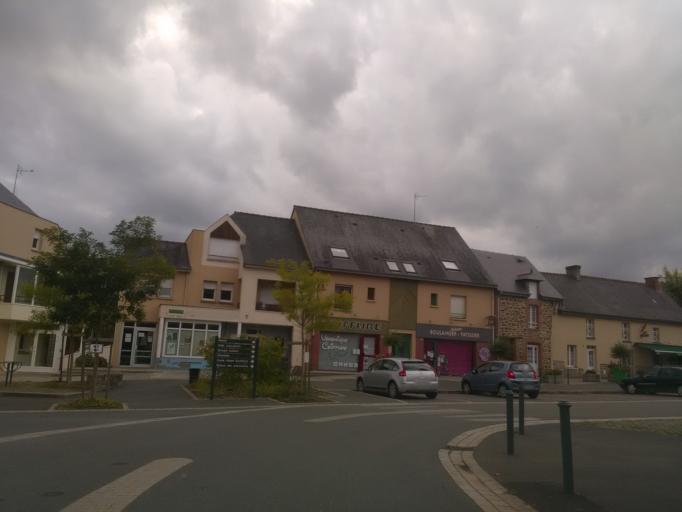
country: FR
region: Brittany
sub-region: Departement d'Ille-et-Vilaine
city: Vignoc
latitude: 48.2482
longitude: -1.7825
